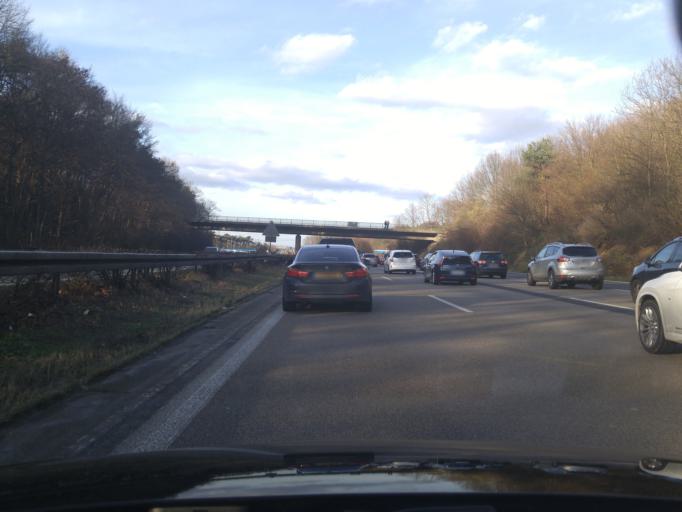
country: DE
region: North Rhine-Westphalia
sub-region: Regierungsbezirk Dusseldorf
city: Hilden
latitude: 51.1542
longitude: 6.9655
